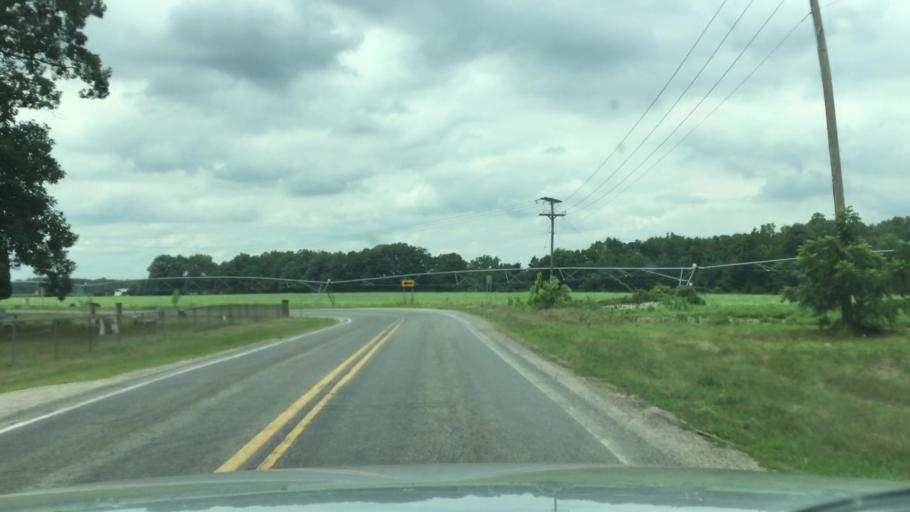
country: US
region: Michigan
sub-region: Saginaw County
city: Burt
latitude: 43.2805
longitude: -83.8878
